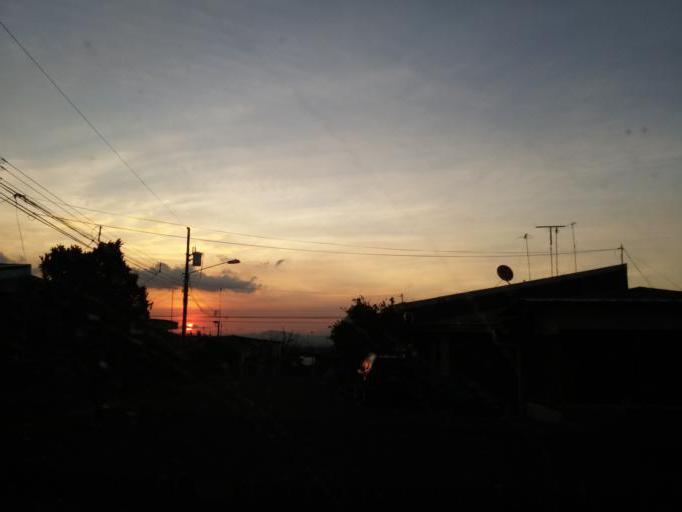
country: CR
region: Alajuela
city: Sabanilla
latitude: 10.0747
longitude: -84.2165
